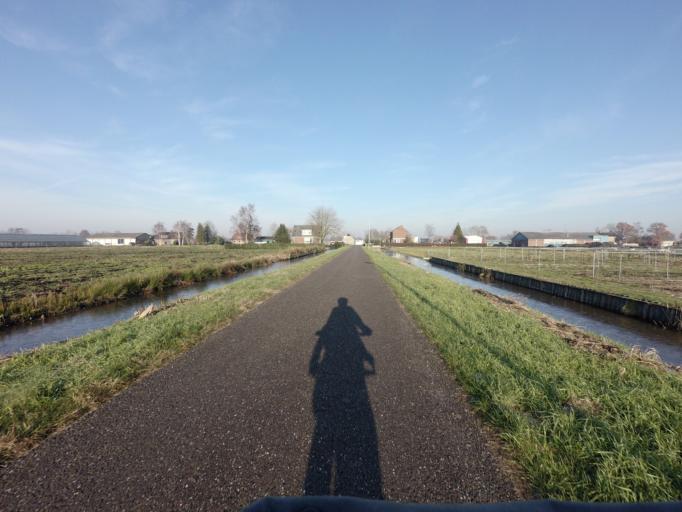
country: NL
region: Utrecht
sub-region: Gemeente De Ronde Venen
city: Mijdrecht
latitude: 52.1702
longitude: 4.8466
